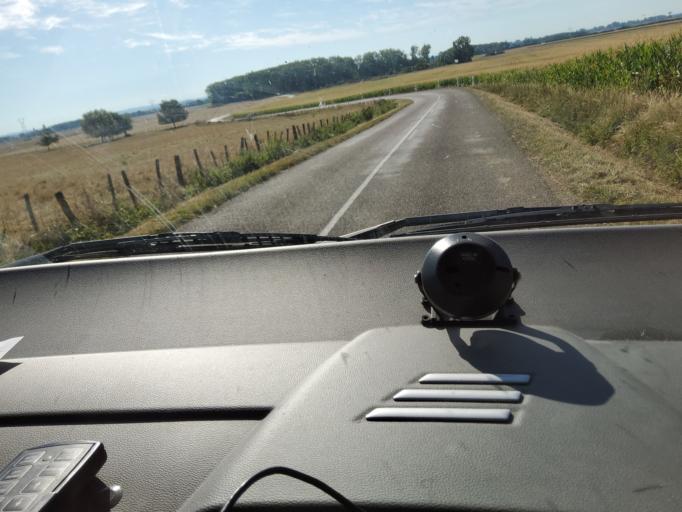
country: FR
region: Bourgogne
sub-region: Departement de la Cote-d'Or
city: Brazey-en-Plaine
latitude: 47.1415
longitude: 5.2486
